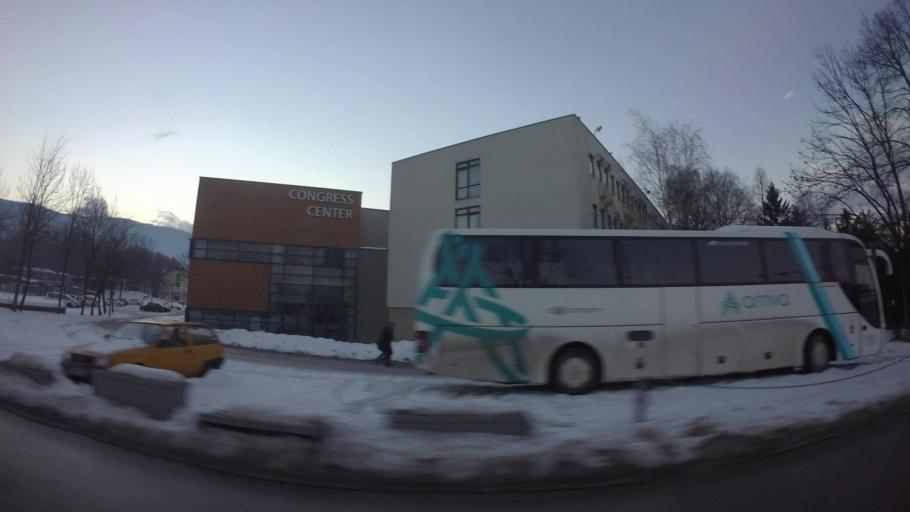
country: BA
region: Federation of Bosnia and Herzegovina
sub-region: Kanton Sarajevo
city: Sarajevo
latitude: 43.8267
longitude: 18.3084
